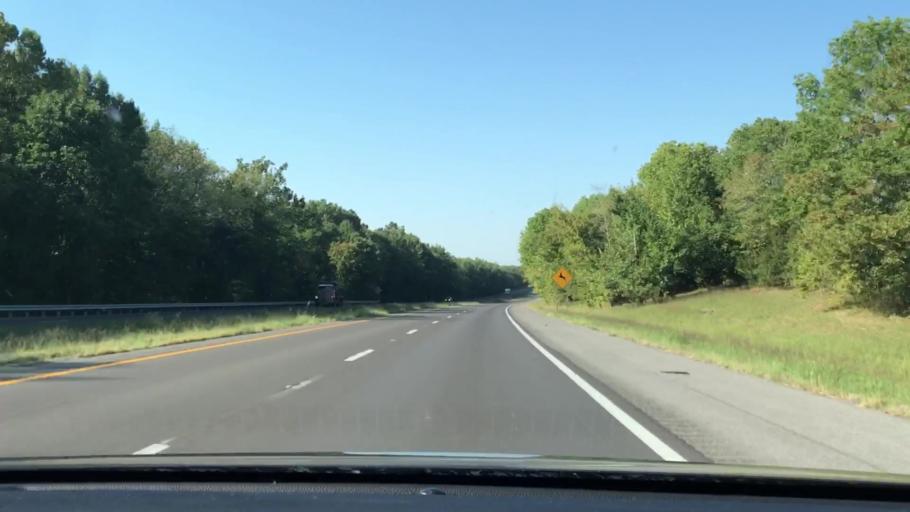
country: US
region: Kentucky
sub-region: Fulton County
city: Fulton
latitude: 36.6035
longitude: -88.7971
